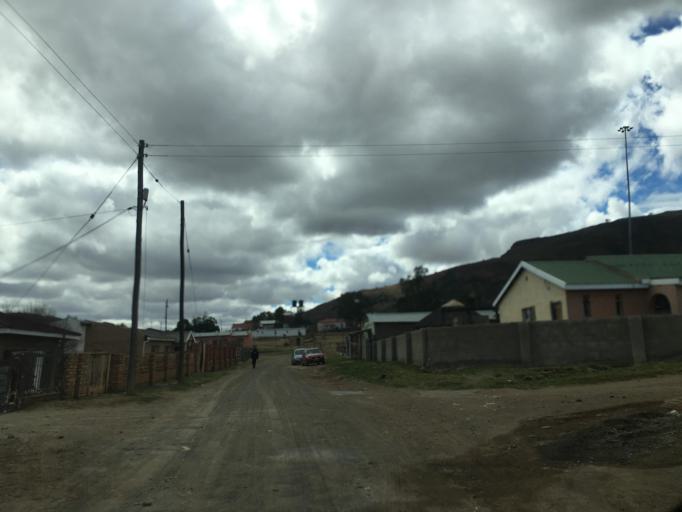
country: ZA
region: Eastern Cape
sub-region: Chris Hani District Municipality
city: Cala
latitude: -31.5301
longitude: 27.6974
